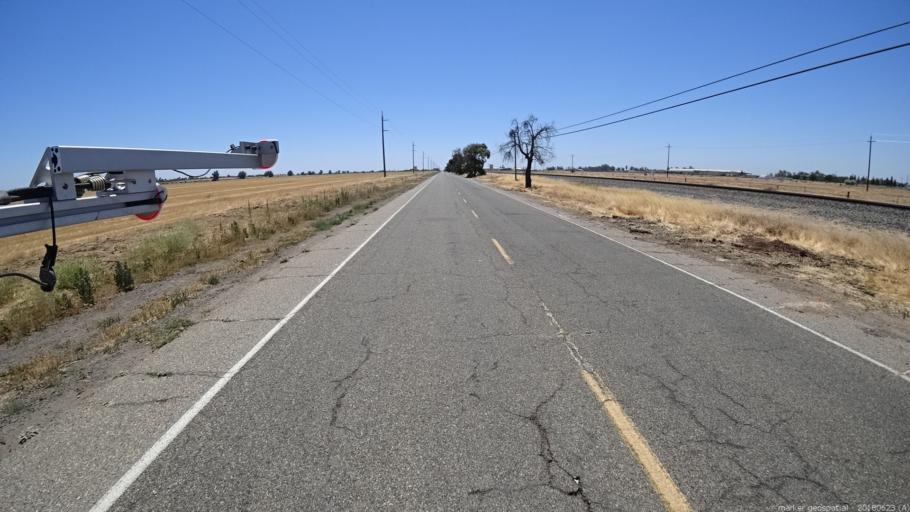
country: US
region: California
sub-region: Madera County
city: Chowchilla
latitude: 37.1169
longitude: -120.2472
